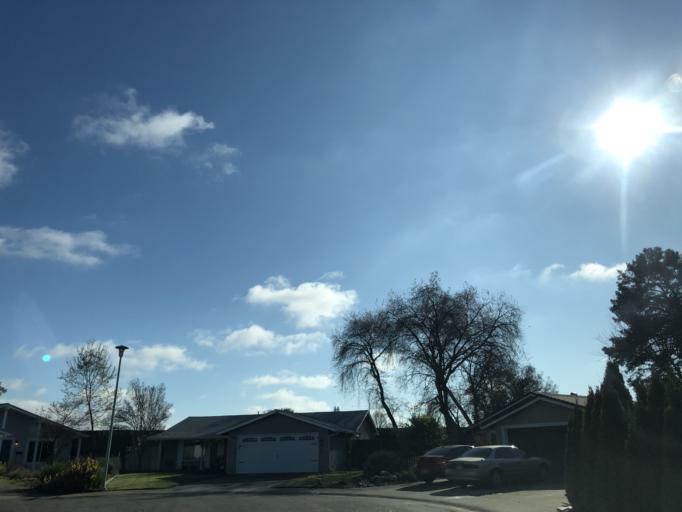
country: US
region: California
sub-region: Sacramento County
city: Rosemont
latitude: 38.5598
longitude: -121.3822
